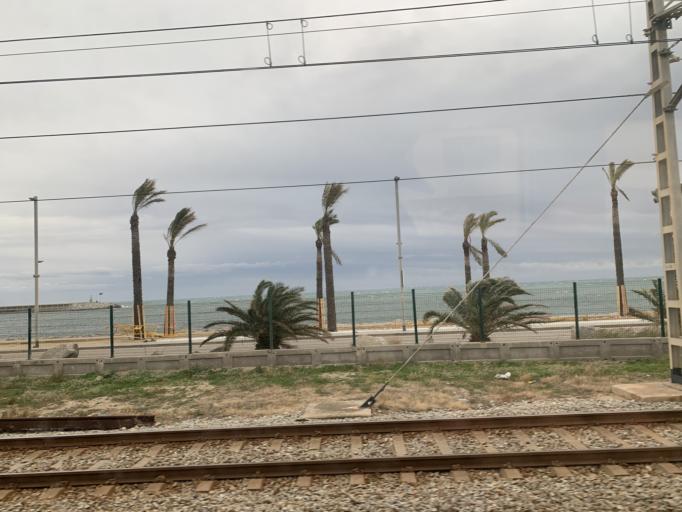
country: ES
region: Catalonia
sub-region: Provincia de Barcelona
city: Mataro
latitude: 41.5282
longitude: 2.4385
